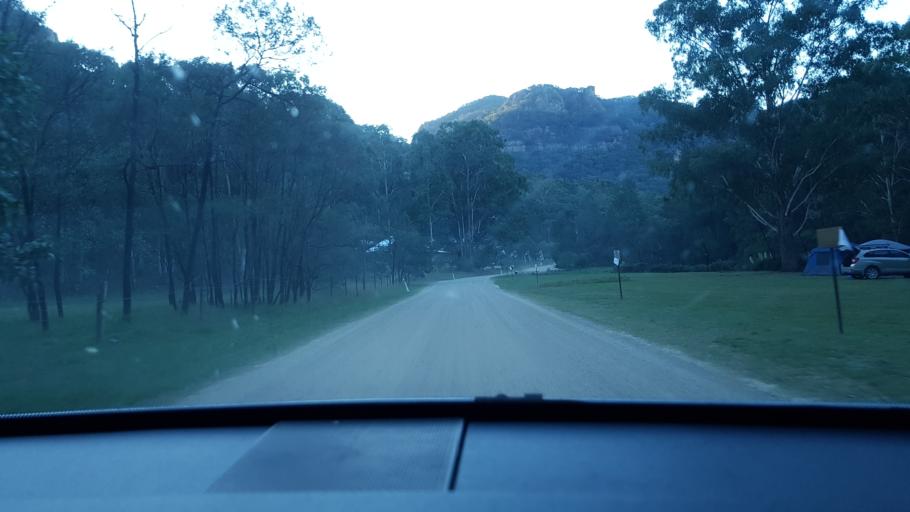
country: AU
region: New South Wales
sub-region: Lithgow
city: Portland
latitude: -33.1809
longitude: 150.2364
